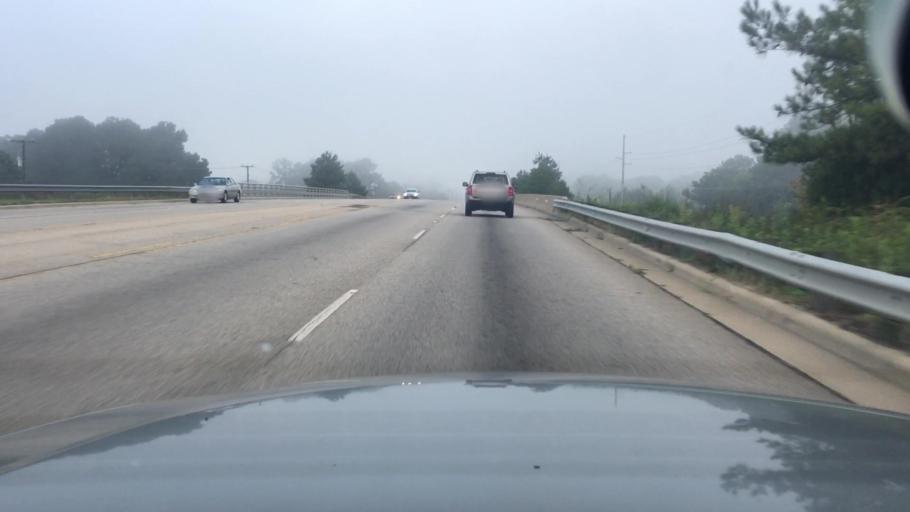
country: US
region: North Carolina
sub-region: Cumberland County
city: Hope Mills
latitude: 35.0173
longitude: -78.9228
